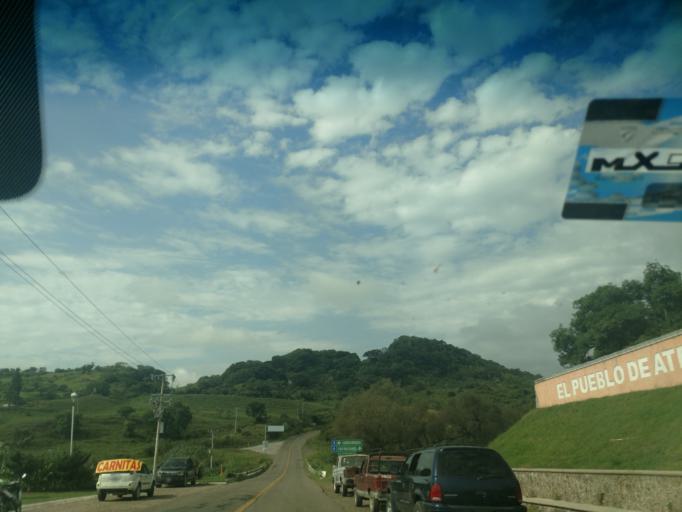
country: MX
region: Jalisco
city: El Salto
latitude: 20.4190
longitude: -104.4996
